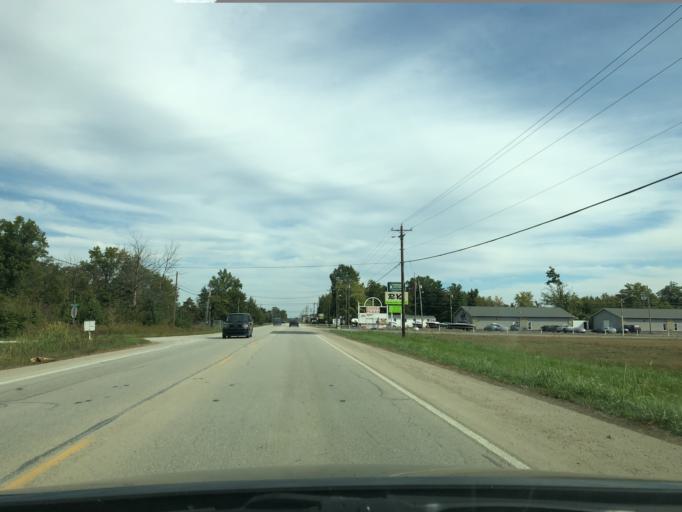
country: US
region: Ohio
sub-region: Clermont County
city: Mount Repose
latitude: 39.2131
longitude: -84.2040
